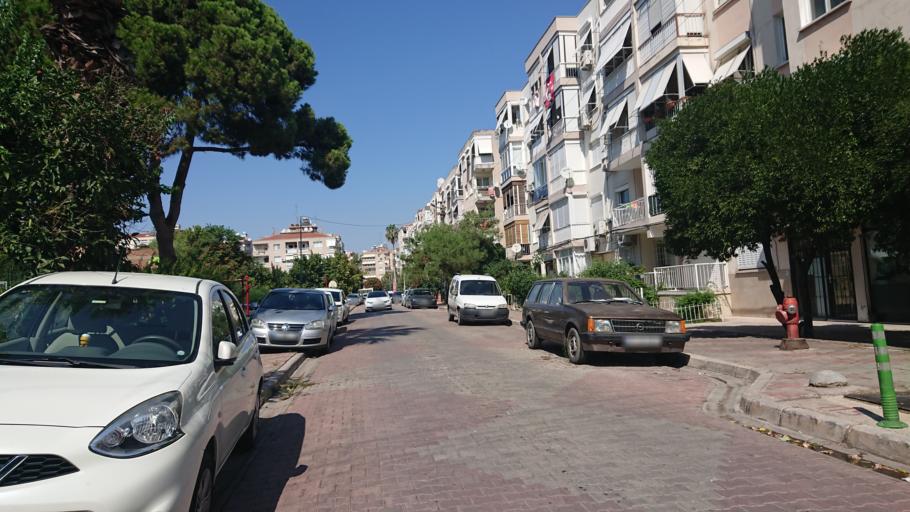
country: TR
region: Izmir
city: Karsiyaka
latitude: 38.4569
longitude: 27.1060
